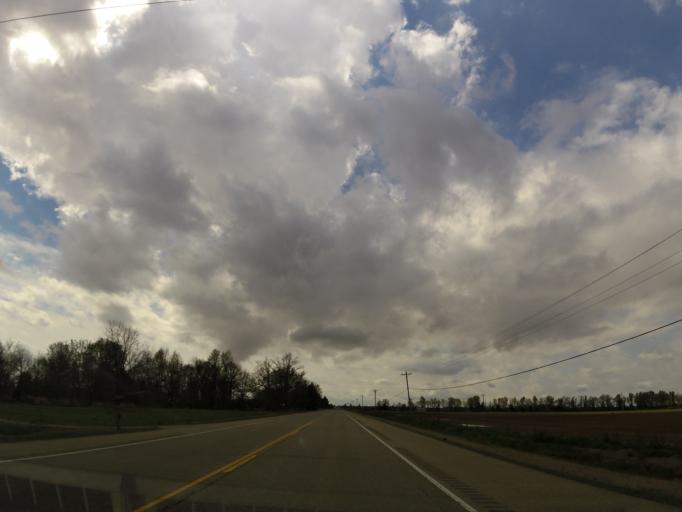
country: US
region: Arkansas
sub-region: Clay County
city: Corning
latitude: 36.4500
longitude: -90.5855
